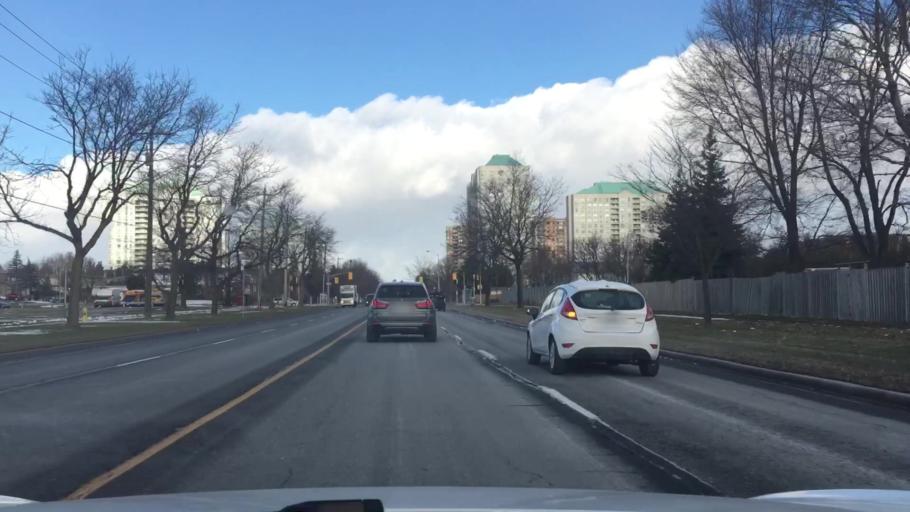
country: CA
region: Ontario
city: Scarborough
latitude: 43.8037
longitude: -79.2647
